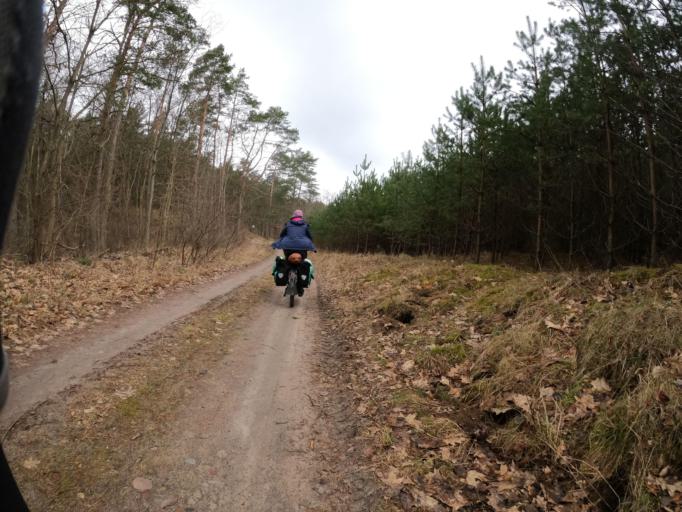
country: PL
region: Greater Poland Voivodeship
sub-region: Powiat zlotowski
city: Sypniewo
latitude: 53.4870
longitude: 16.5374
